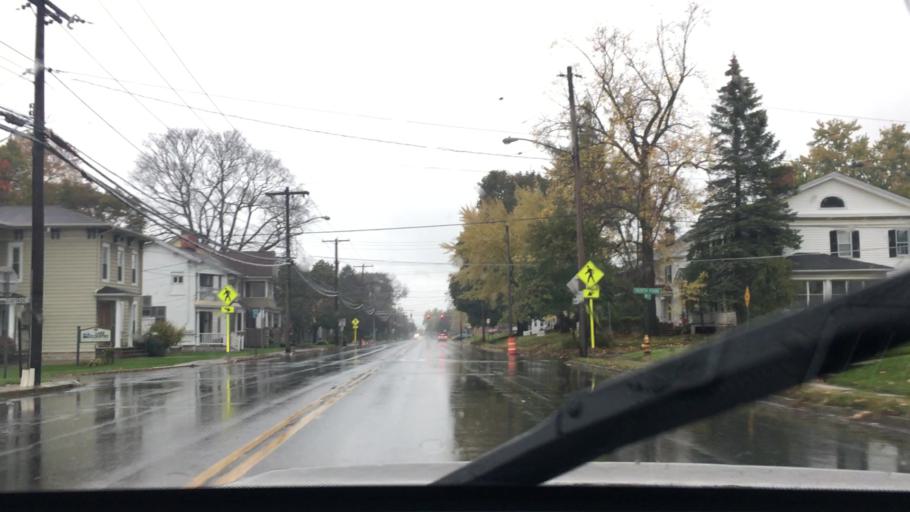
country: US
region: New York
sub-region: Cayuga County
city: Auburn
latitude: 42.9388
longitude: -76.5666
